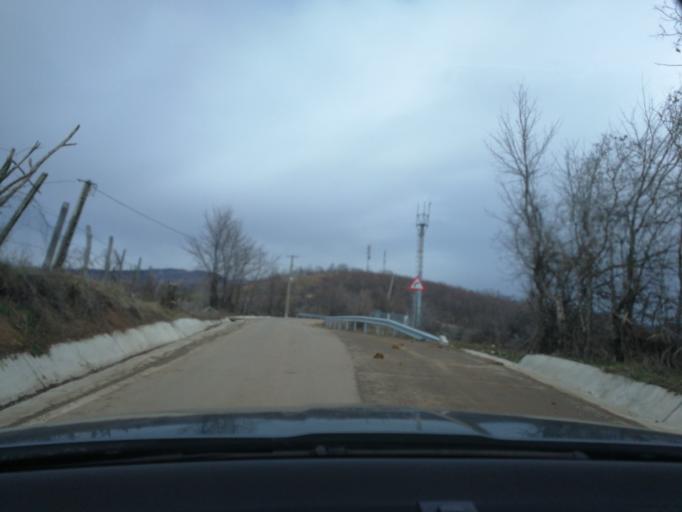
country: RO
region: Dambovita
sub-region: Comuna Buciumeni
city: Buciumeni
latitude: 45.1393
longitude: 25.4586
